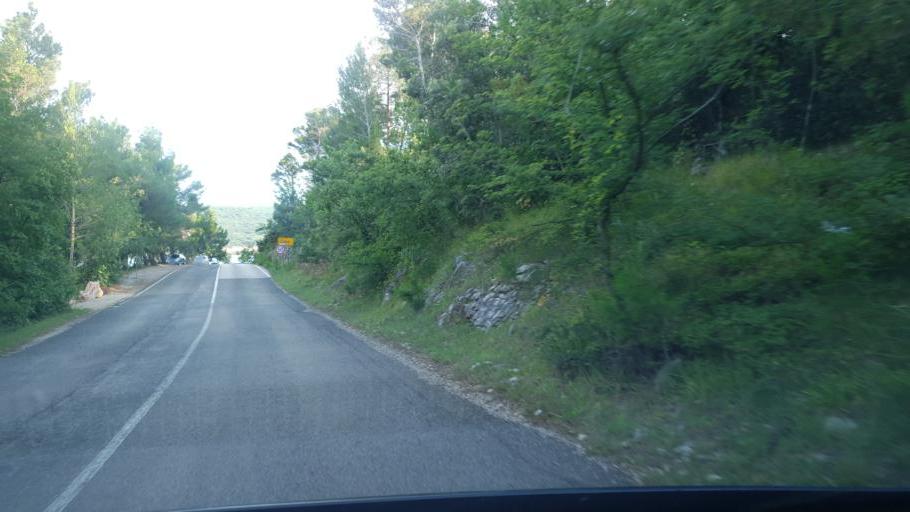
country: HR
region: Primorsko-Goranska
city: Njivice
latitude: 45.1611
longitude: 14.6020
